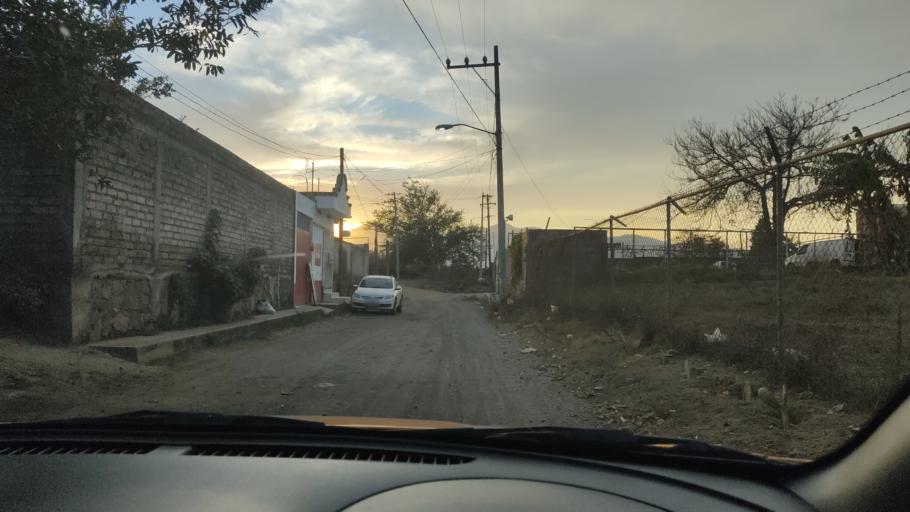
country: MX
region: Nayarit
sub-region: Tepic
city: La Corregidora
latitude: 21.4617
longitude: -104.8286
